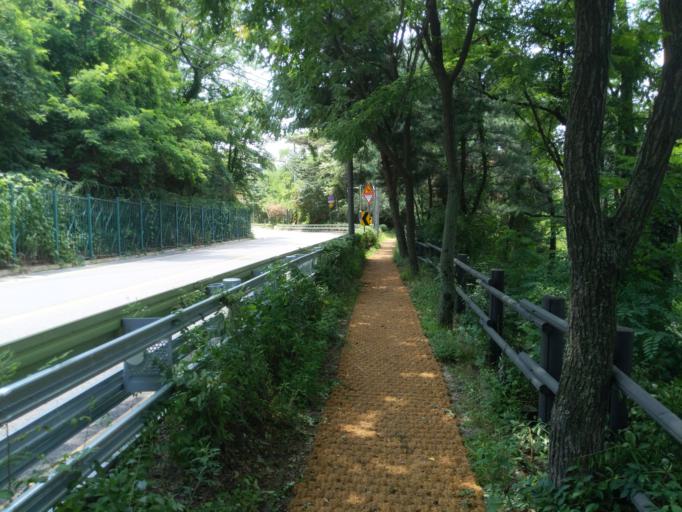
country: KR
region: Seoul
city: Seoul
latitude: 37.5974
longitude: 126.9740
